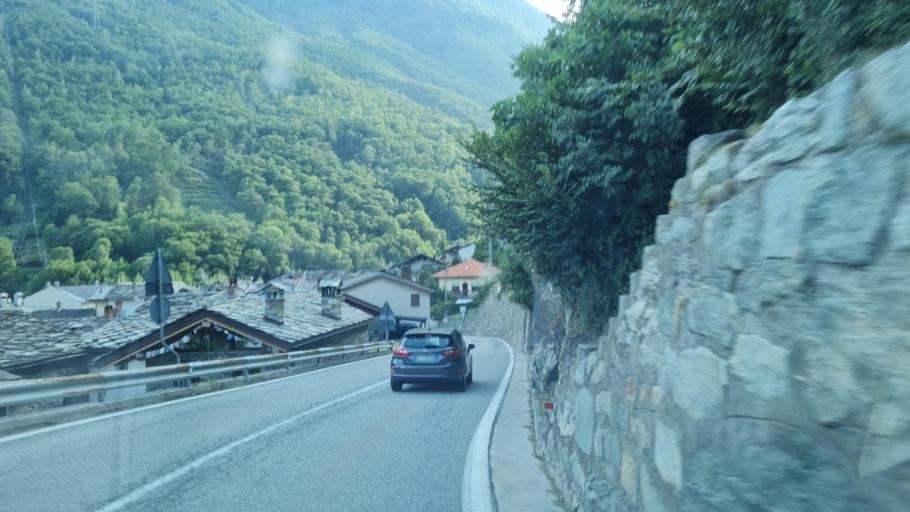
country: IT
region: Aosta Valley
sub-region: Valle d'Aosta
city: Hone
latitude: 45.6139
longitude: 7.7346
